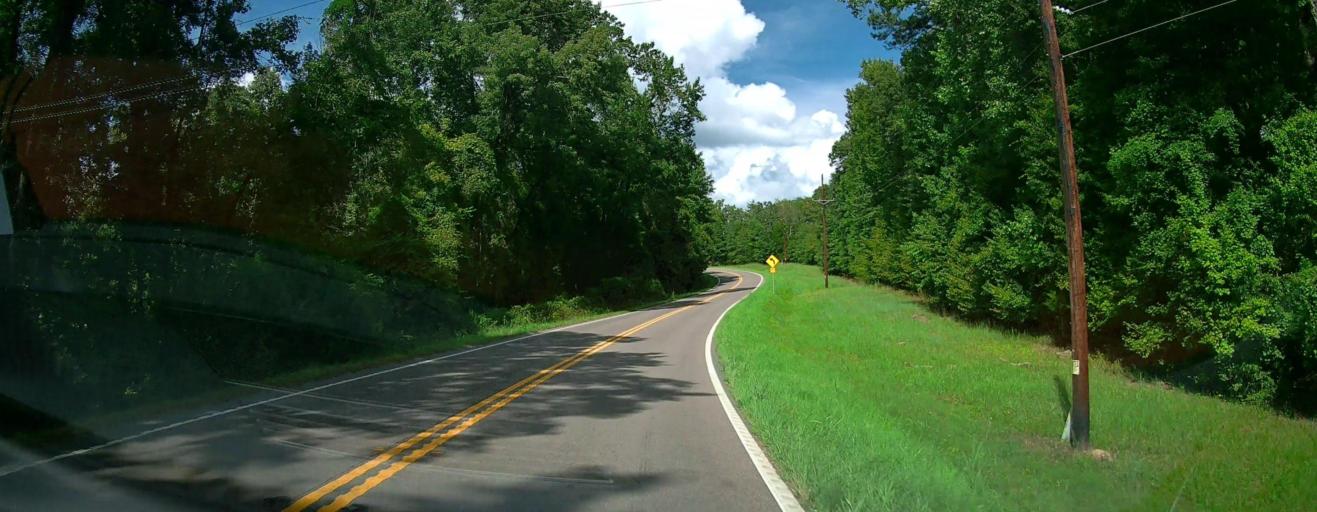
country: US
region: Georgia
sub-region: Talbot County
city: Talbotton
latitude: 32.6223
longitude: -84.4884
